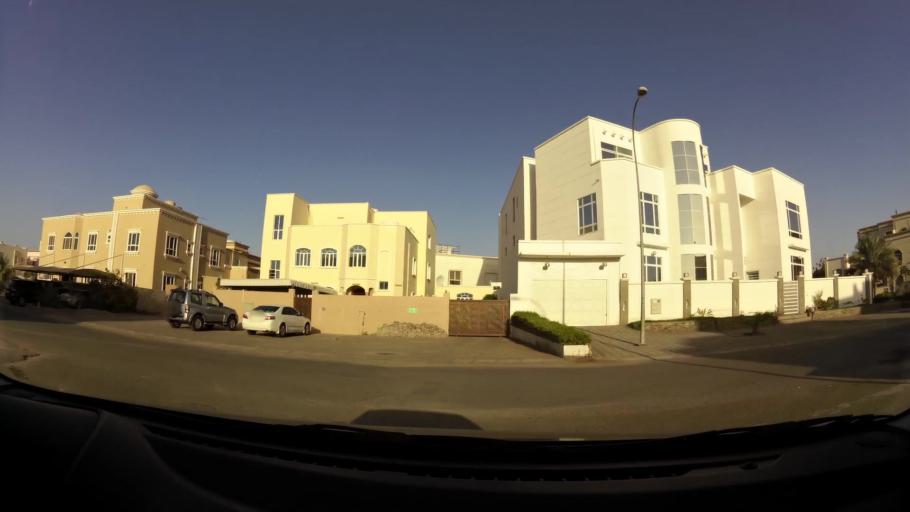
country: OM
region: Muhafazat Masqat
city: As Sib al Jadidah
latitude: 23.6104
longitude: 58.2342
